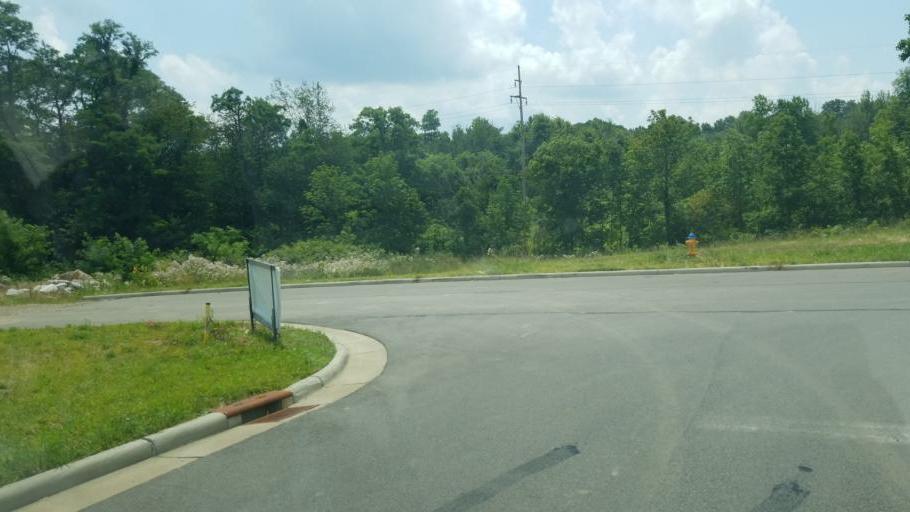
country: US
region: Ohio
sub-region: Richland County
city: Ontario
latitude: 40.7803
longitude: -82.5859
